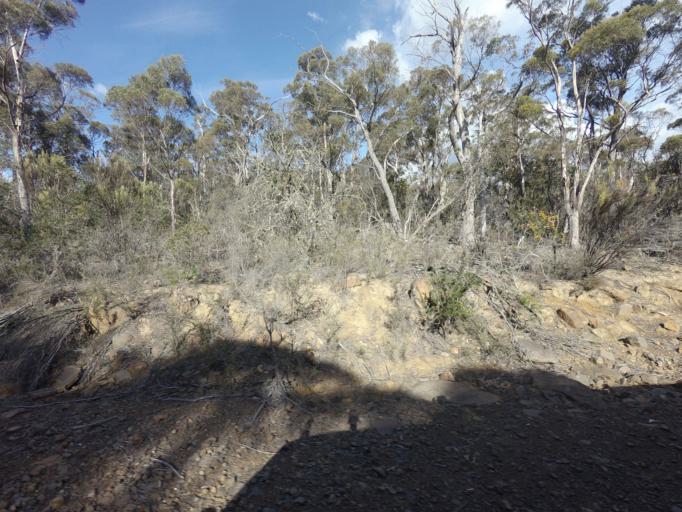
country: AU
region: Tasmania
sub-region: Break O'Day
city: St Helens
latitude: -41.8609
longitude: 148.0236
